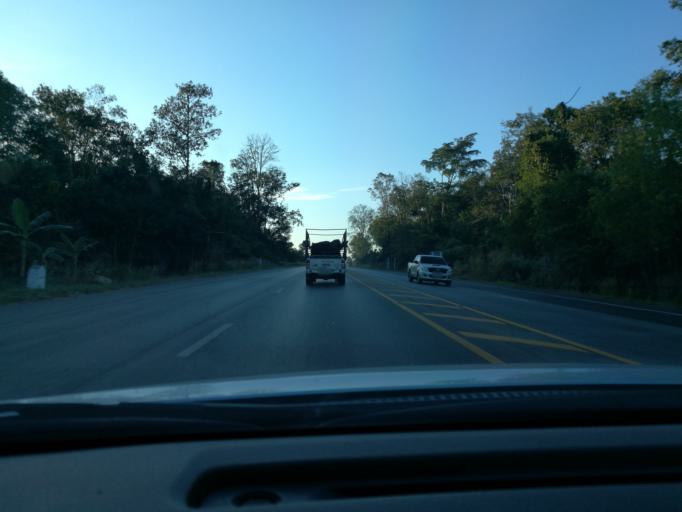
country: TH
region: Phitsanulok
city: Wang Thong
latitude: 16.8454
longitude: 100.5275
